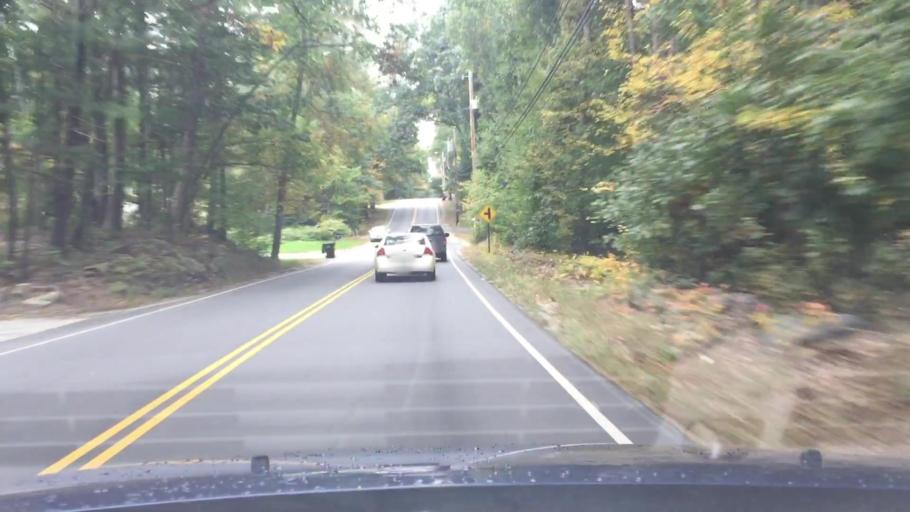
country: US
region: Massachusetts
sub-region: Middlesex County
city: Tyngsboro
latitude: 42.7033
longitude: -71.3925
